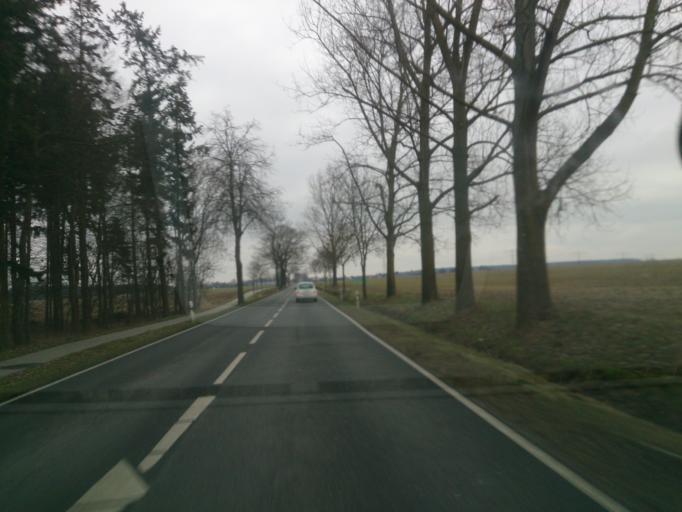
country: DE
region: Mecklenburg-Vorpommern
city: Demmin
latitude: 53.8781
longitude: 13.0228
